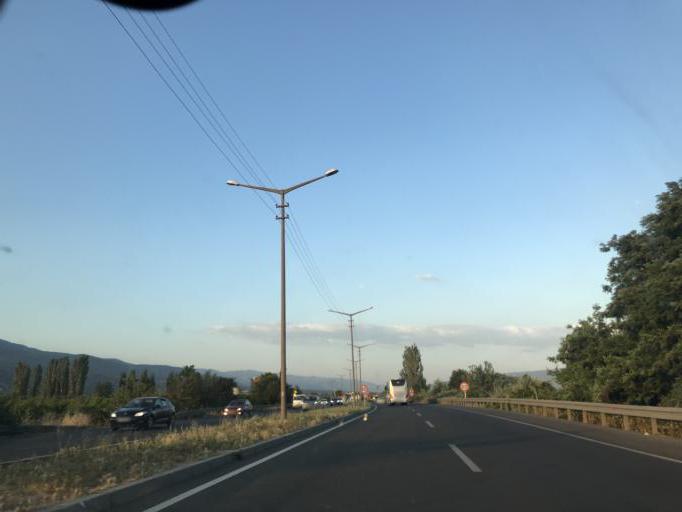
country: TR
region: Aydin
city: Pamukoren
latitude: 37.9046
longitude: 28.5525
